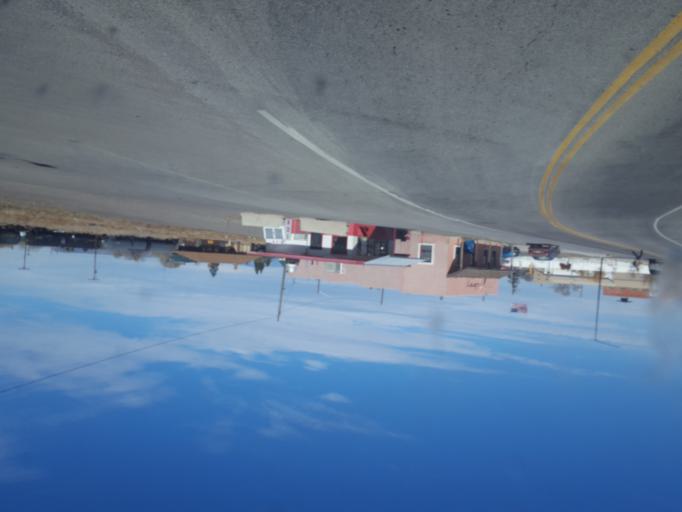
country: US
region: Colorado
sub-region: Conejos County
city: Conejos
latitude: 37.0730
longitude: -106.0090
